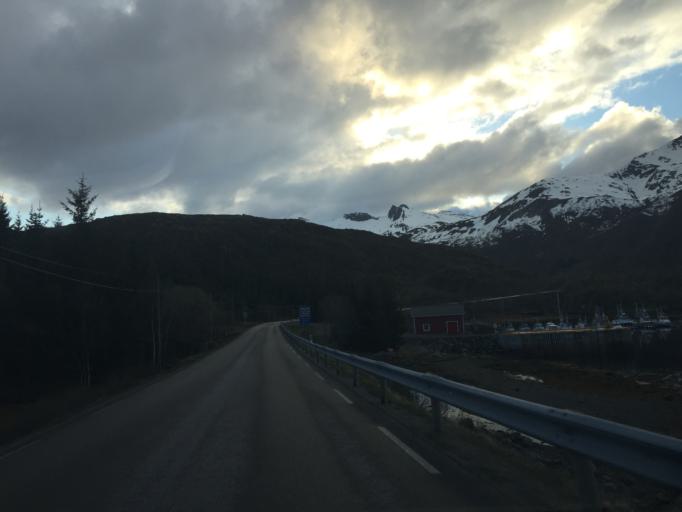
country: NO
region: Nordland
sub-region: Vagan
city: Svolvaer
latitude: 68.3185
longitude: 14.7061
